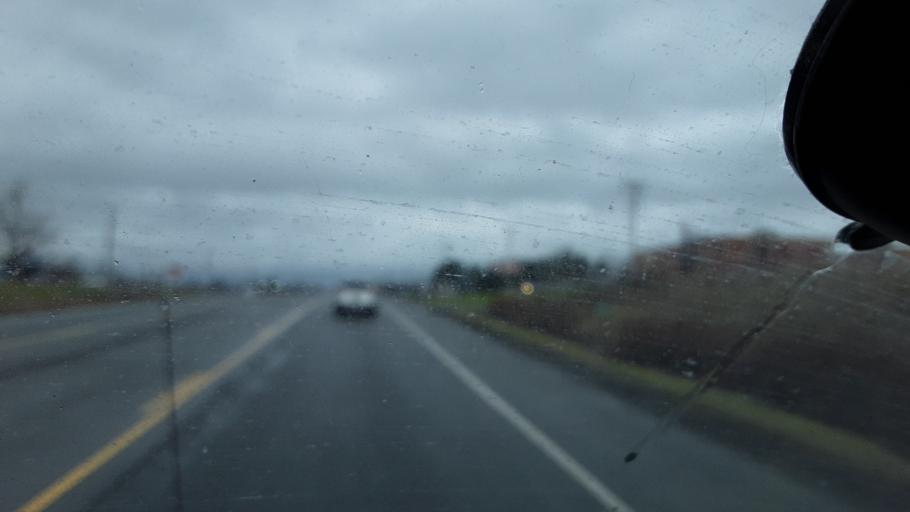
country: US
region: New York
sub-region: Cattaraugus County
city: Yorkshire
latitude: 42.5364
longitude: -78.4784
